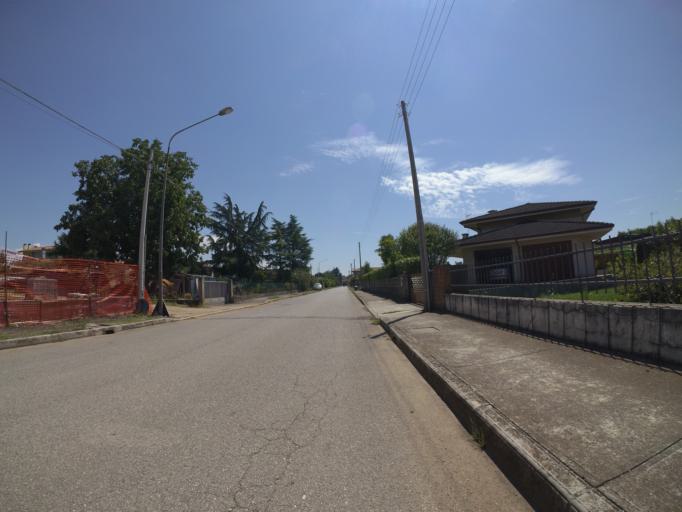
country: IT
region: Friuli Venezia Giulia
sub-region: Provincia di Udine
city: Talmassons
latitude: 45.9333
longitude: 13.1167
